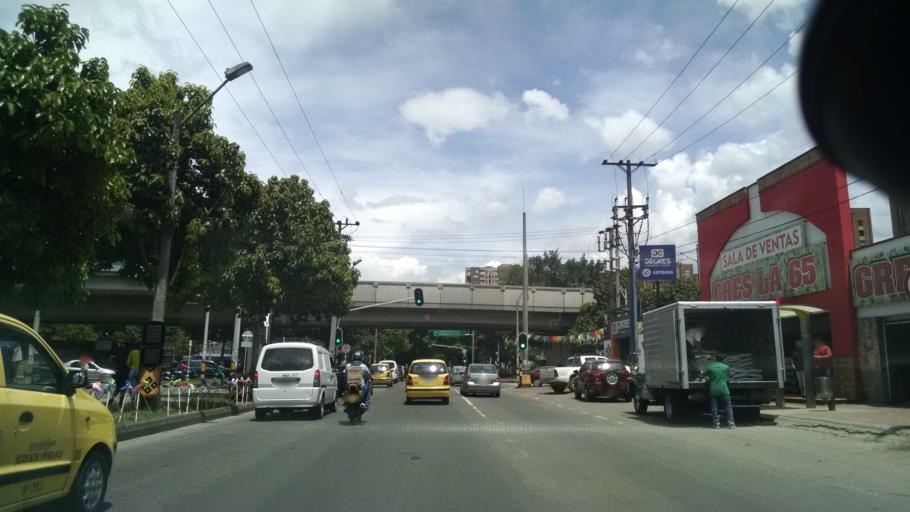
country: CO
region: Antioquia
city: Medellin
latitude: 6.2522
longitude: -75.5827
